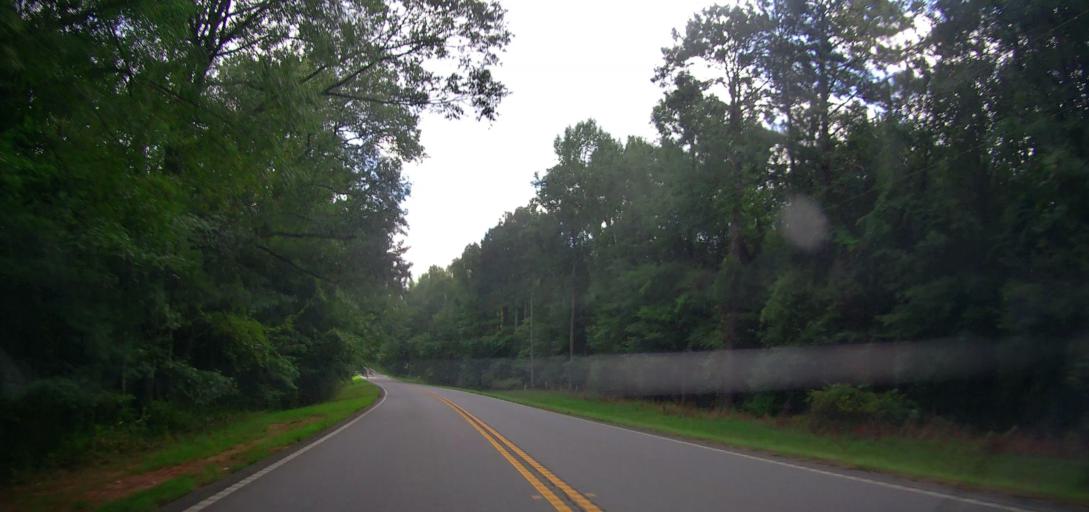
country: US
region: Georgia
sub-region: Talbot County
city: Talbotton
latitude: 32.6296
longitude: -84.4885
